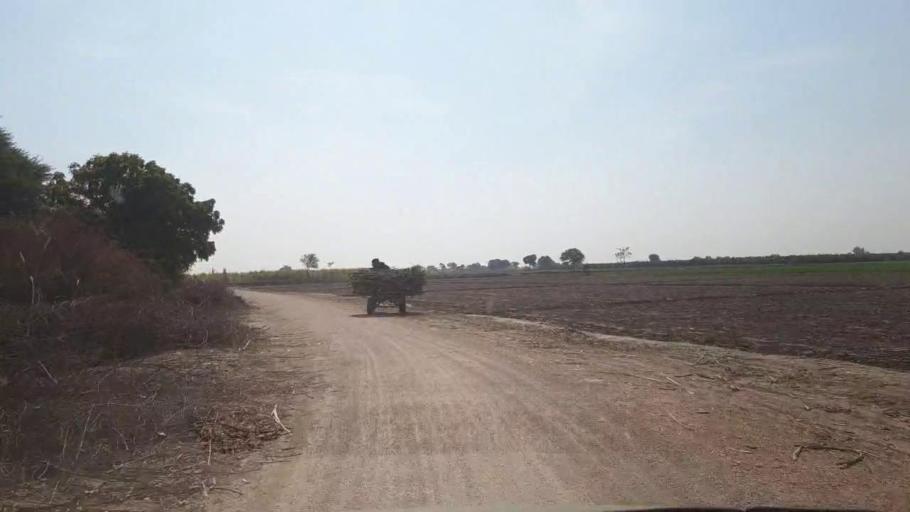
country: PK
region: Sindh
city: Chambar
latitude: 25.3466
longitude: 68.8356
